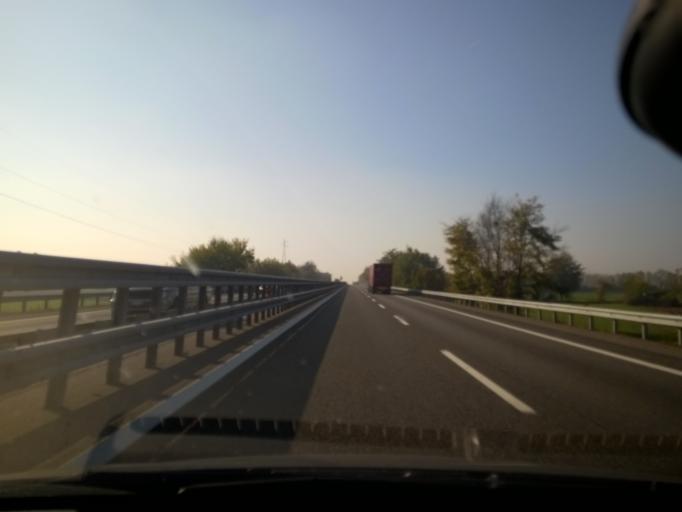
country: IT
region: Lombardy
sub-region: Provincia di Pavia
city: Santa Giuletta
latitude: 45.0486
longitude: 9.1701
